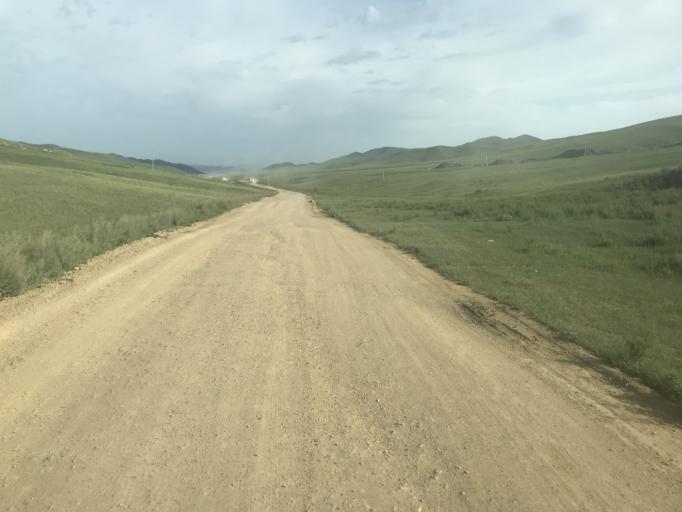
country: MN
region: Central Aimak
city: Javhlant
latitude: 48.7323
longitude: 106.1334
